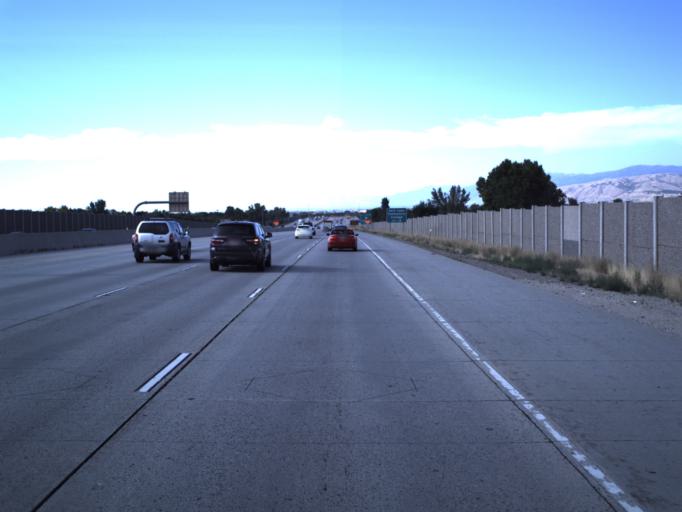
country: US
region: Utah
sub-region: Salt Lake County
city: Taylorsville
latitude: 40.6538
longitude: -111.9524
